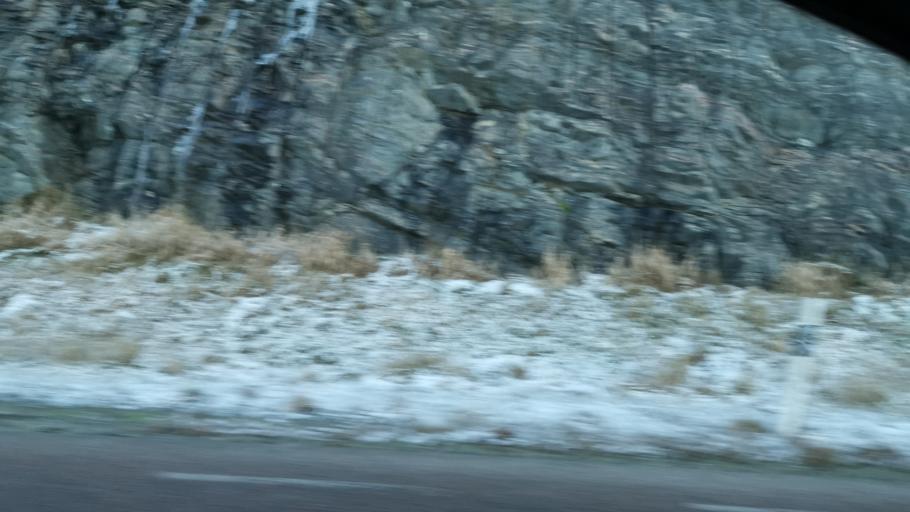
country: SE
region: Vaestra Goetaland
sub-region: Munkedals Kommun
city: Munkedal
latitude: 58.4100
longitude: 11.7350
